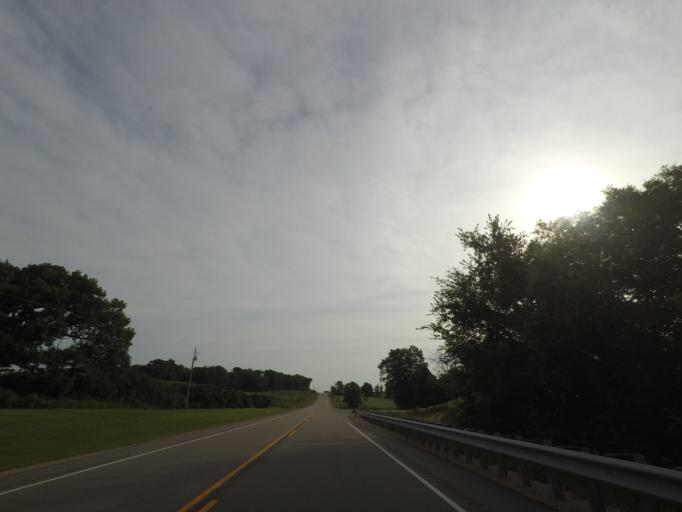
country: US
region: Wisconsin
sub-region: Columbia County
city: Lodi
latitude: 43.3248
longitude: -89.4909
